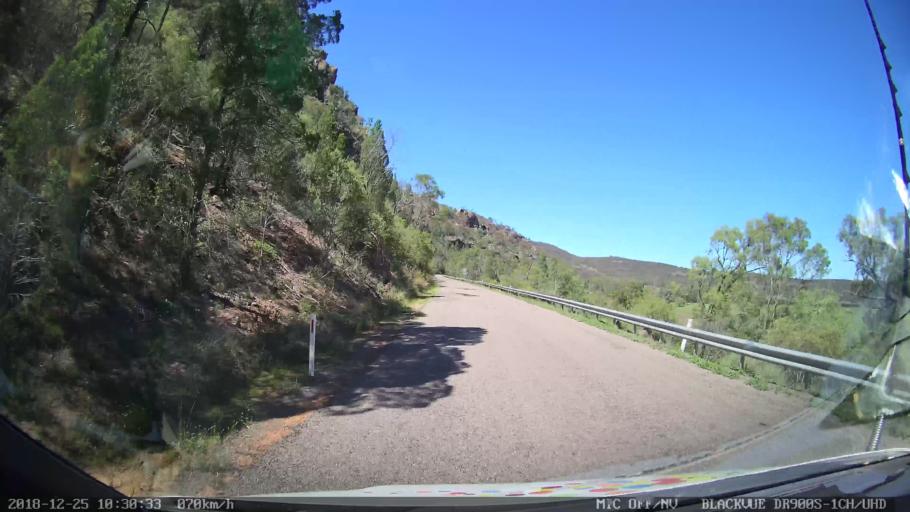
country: AU
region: New South Wales
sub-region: Muswellbrook
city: Denman
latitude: -32.3825
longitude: 150.4369
